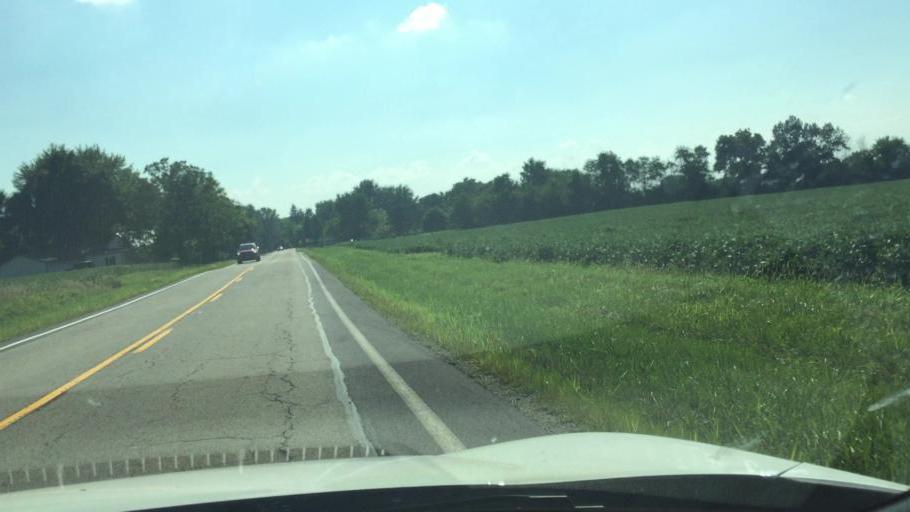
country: US
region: Ohio
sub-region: Champaign County
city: Mechanicsburg
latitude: 40.0817
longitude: -83.6315
